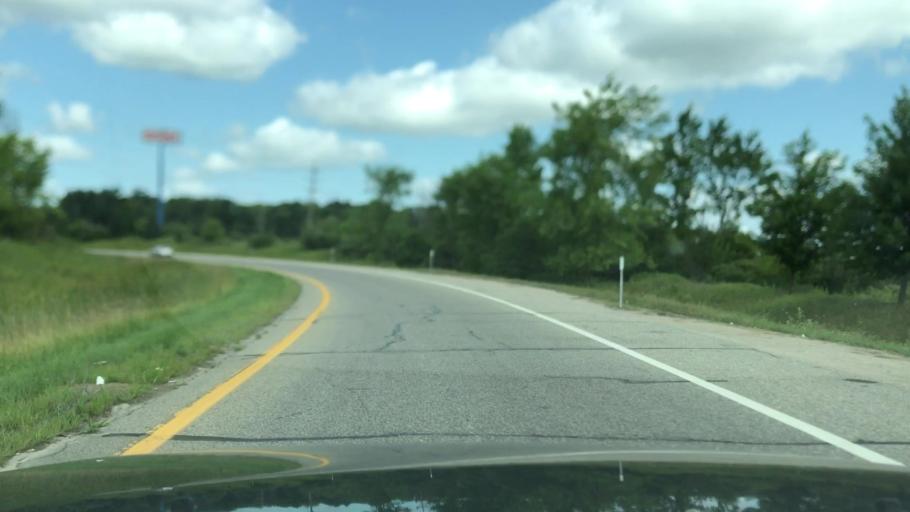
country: US
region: Michigan
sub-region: Mecosta County
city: Big Rapids
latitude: 43.6880
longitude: -85.5182
